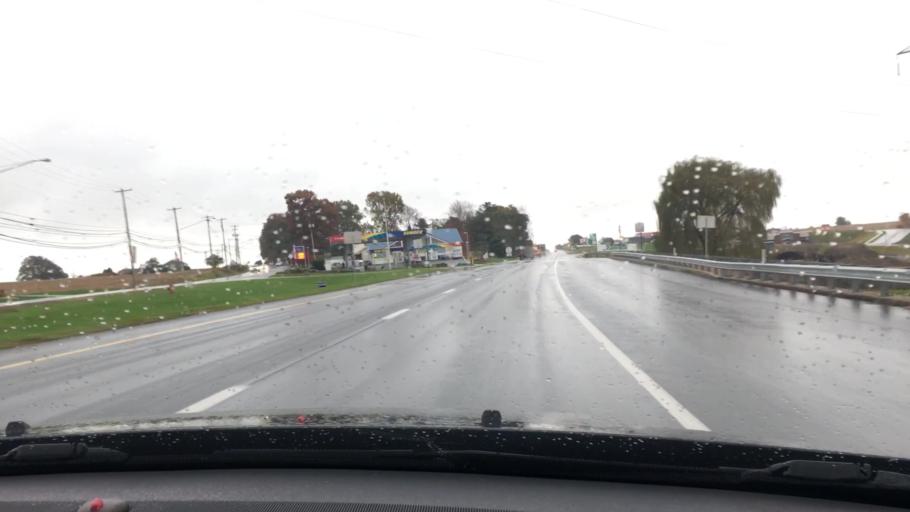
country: US
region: Pennsylvania
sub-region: Lancaster County
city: Willow Street
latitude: 39.9914
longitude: -76.2855
